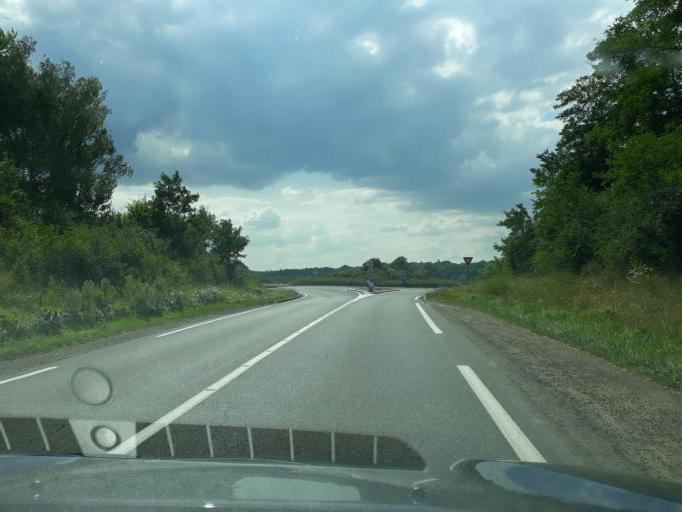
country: FR
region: Centre
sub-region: Departement du Cher
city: Cours-les-Barres
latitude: 47.0118
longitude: 3.0387
